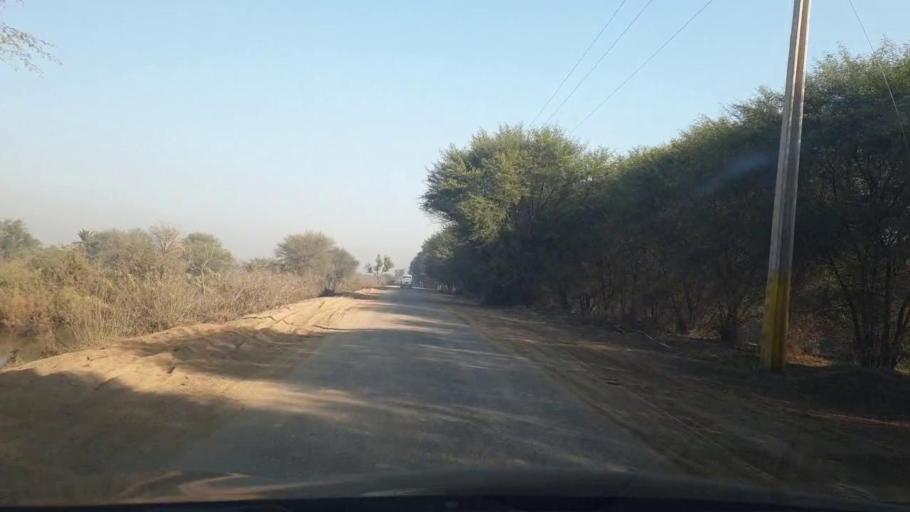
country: PK
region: Sindh
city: Mirpur Mathelo
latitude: 28.0640
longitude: 69.4648
